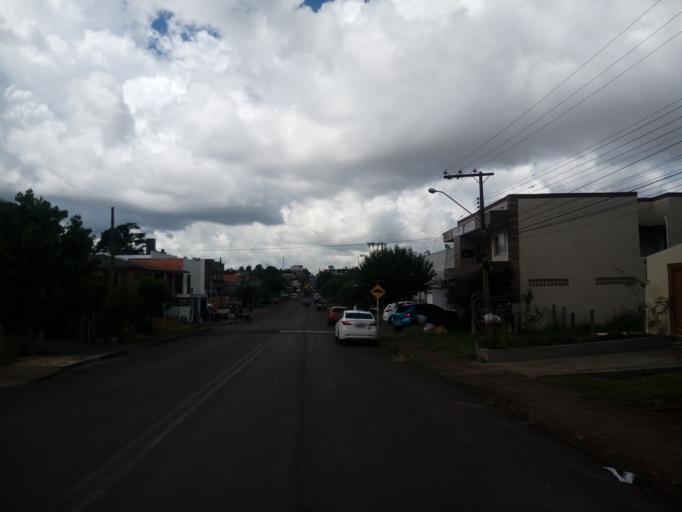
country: BR
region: Santa Catarina
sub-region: Chapeco
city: Chapeco
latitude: -27.0765
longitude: -52.6099
